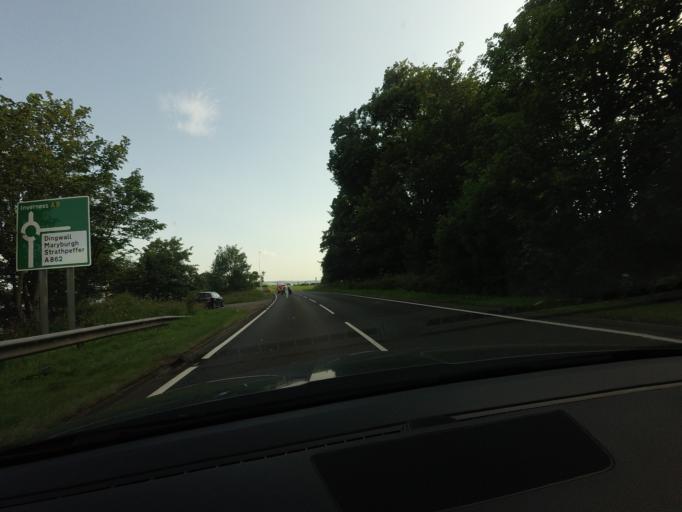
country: GB
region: Scotland
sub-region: Highland
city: Evanton
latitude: 57.6292
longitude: -4.3670
